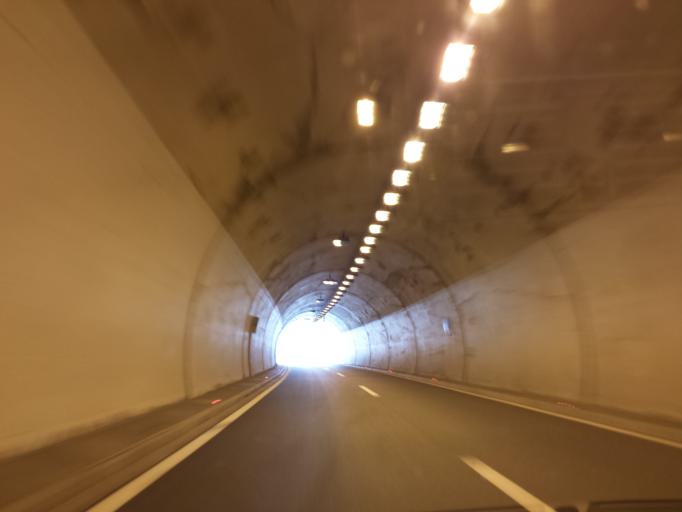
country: HR
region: Zadarska
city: Pridraga
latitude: 44.2573
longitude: 15.5913
